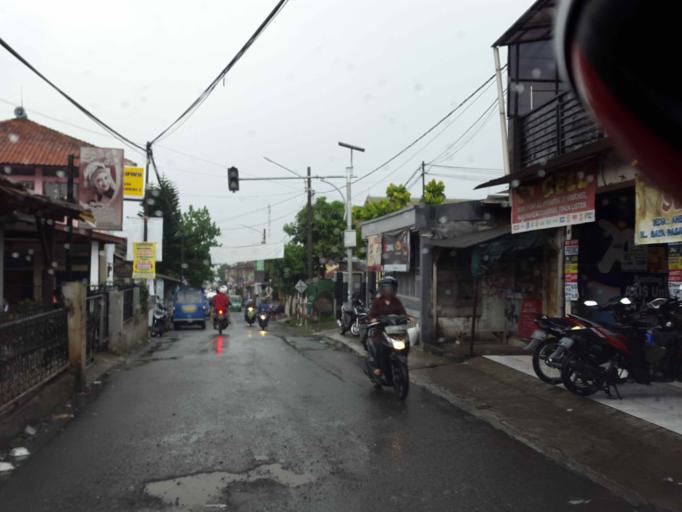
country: ID
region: West Java
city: Cimahi
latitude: -6.8745
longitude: 107.5606
